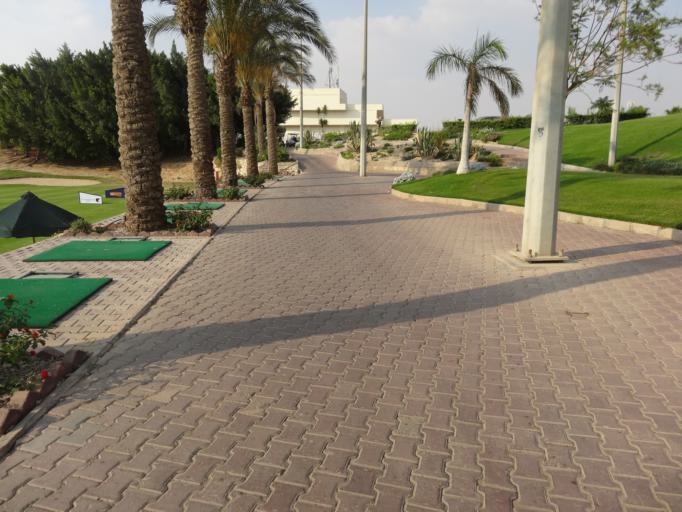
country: EG
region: Muhafazat al Qalyubiyah
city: Al Khankah
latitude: 30.0700
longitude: 31.4339
